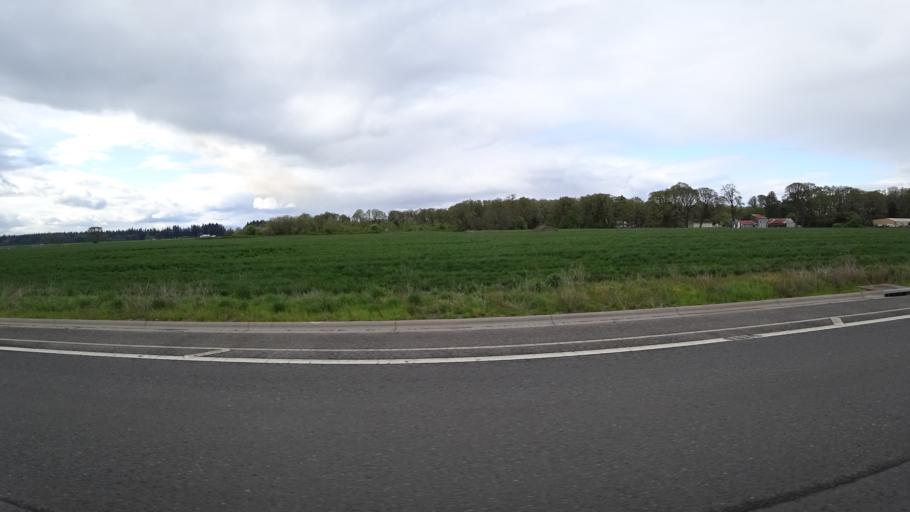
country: US
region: Oregon
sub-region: Washington County
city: Hillsboro
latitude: 45.5528
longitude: -122.9608
